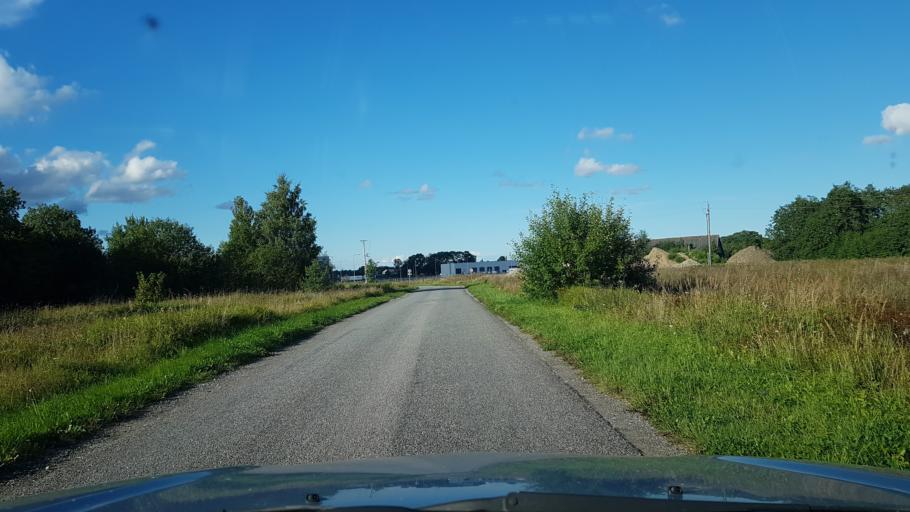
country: EE
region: Harju
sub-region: Kiili vald
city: Kiili
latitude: 59.3322
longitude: 24.8331
